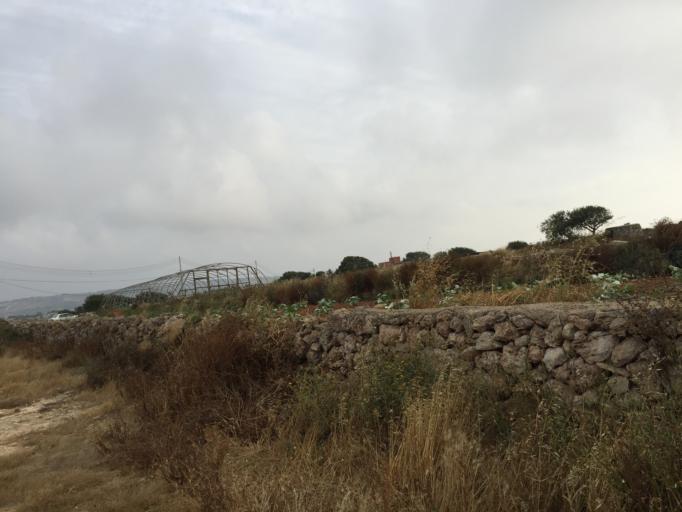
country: MT
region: L-Imgarr
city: Imgarr
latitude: 35.9328
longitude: 14.3864
